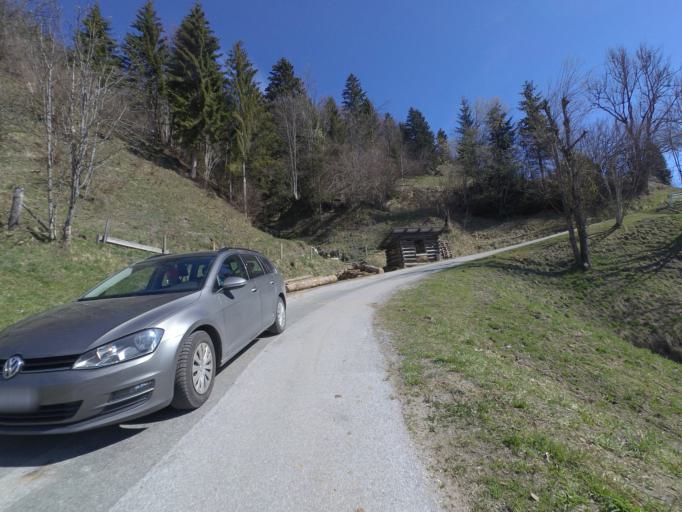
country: AT
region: Salzburg
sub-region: Politischer Bezirk Sankt Johann im Pongau
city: Sankt Veit im Pongau
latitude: 47.3394
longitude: 13.1465
